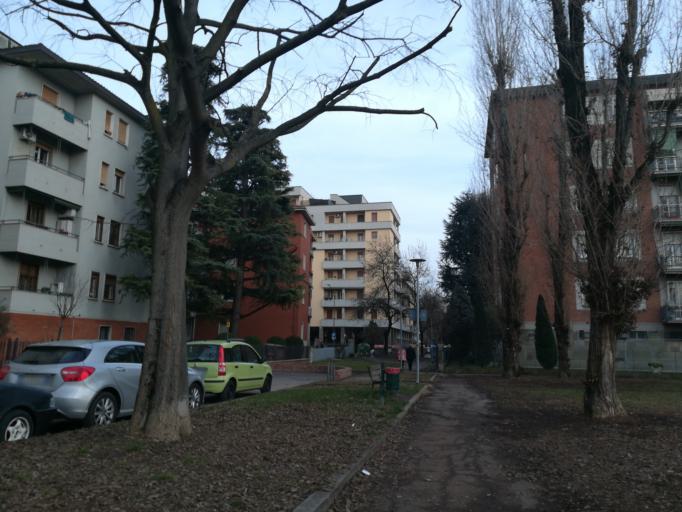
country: IT
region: Emilia-Romagna
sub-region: Provincia di Bologna
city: Progresso
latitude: 44.5457
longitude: 11.3554
